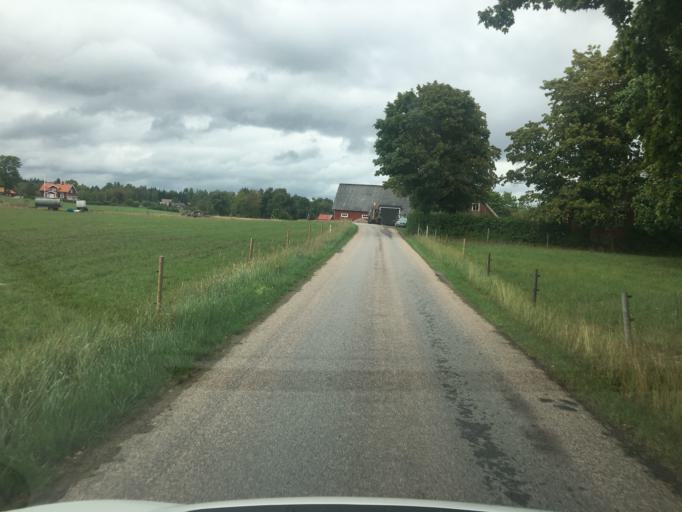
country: SE
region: Kronoberg
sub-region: Ljungby Kommun
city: Lagan
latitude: 56.9279
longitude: 14.0250
